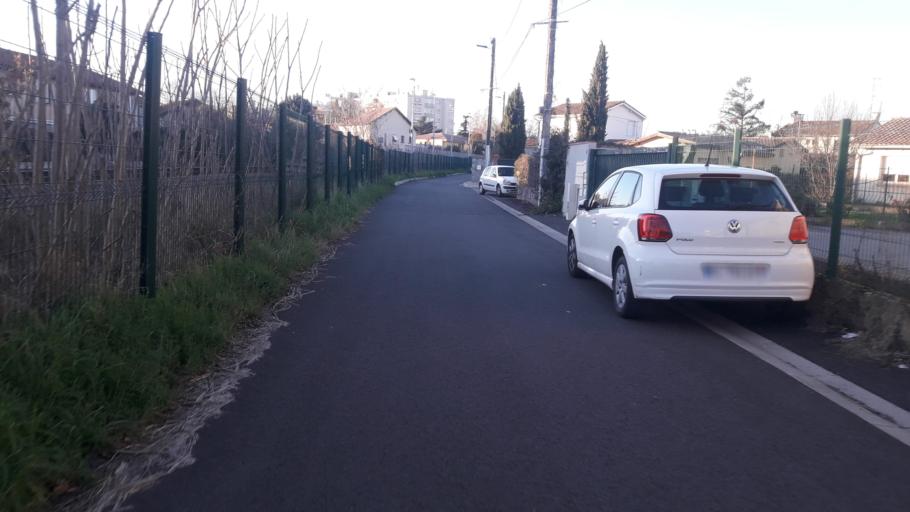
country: FR
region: Midi-Pyrenees
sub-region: Departement de la Haute-Garonne
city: Toulouse
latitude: 43.5717
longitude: 1.4207
